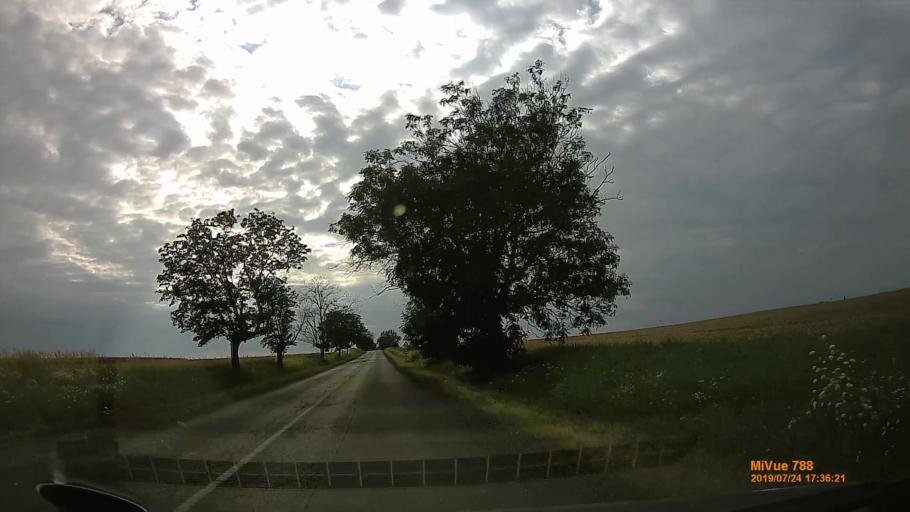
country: HU
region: Borsod-Abauj-Zemplen
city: Abaujszanto
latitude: 48.3131
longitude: 21.1735
